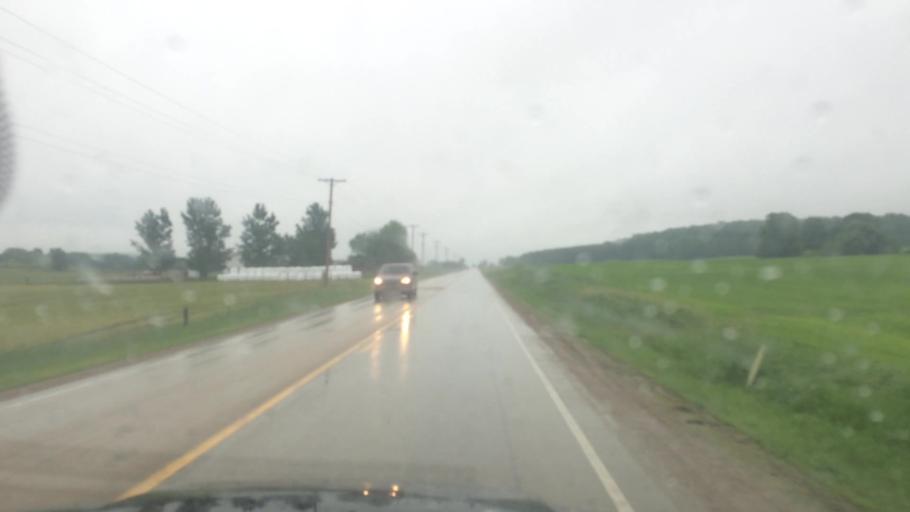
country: US
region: Wisconsin
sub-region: Waupaca County
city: Marion
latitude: 44.6102
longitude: -88.8986
